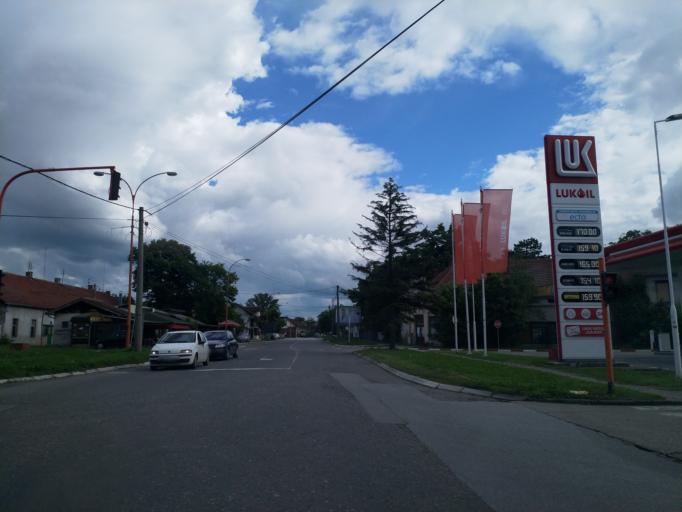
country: RS
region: Central Serbia
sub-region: Pomoravski Okrug
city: Cuprija
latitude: 43.9200
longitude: 21.3744
